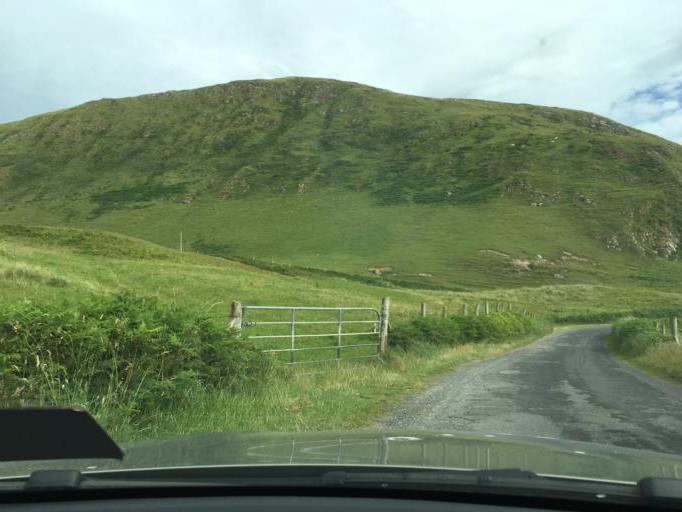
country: IE
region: Ulster
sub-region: County Donegal
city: Carndonagh
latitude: 55.3208
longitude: -7.3226
